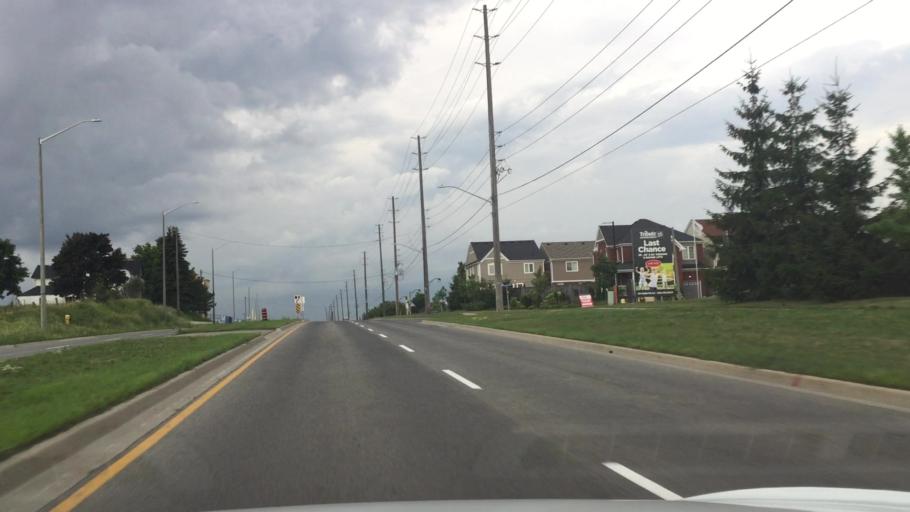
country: CA
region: Ontario
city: Oshawa
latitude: 43.9435
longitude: -78.8323
